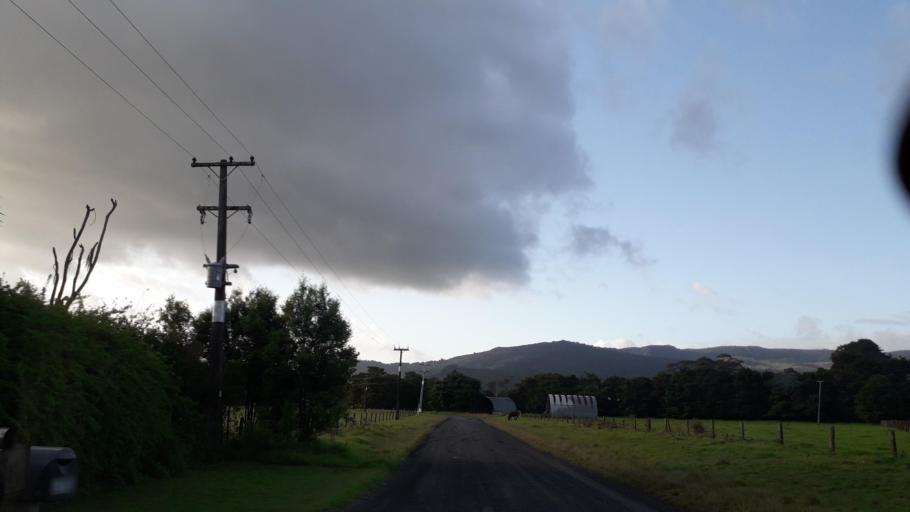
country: NZ
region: Northland
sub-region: Far North District
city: Waimate North
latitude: -35.5022
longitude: 173.6992
